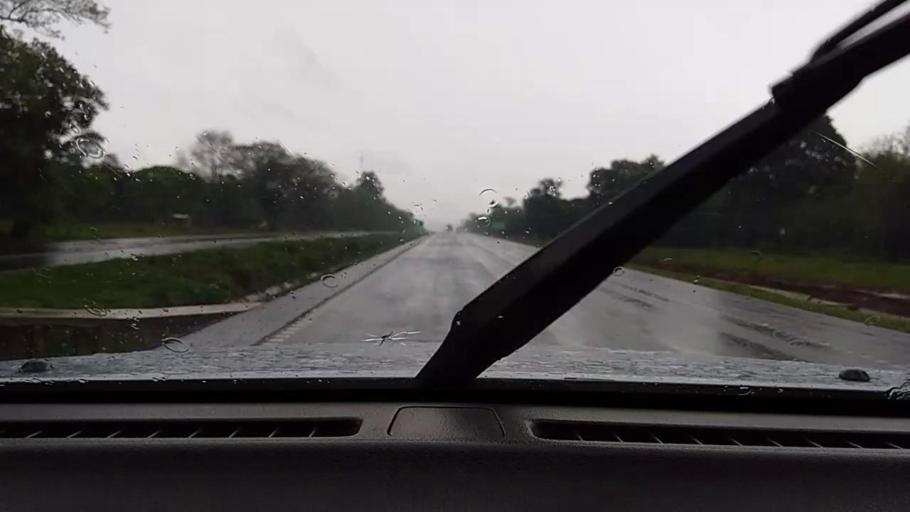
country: PY
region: Caaguazu
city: Repatriacion
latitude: -25.4510
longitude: -55.9012
